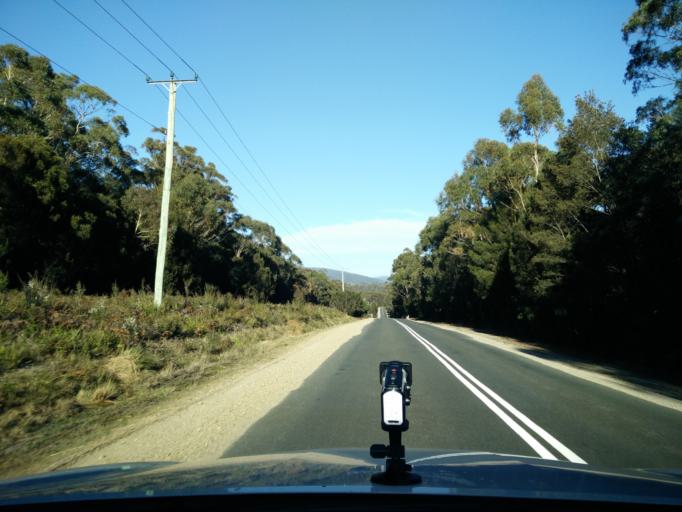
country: AU
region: Tasmania
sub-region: Break O'Day
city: St Helens
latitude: -41.2944
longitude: 148.1903
